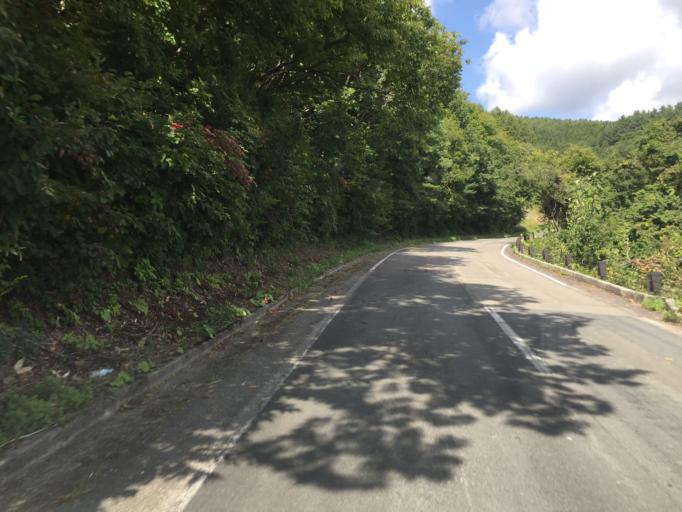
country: JP
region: Fukushima
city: Inawashiro
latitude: 37.5896
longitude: 140.0301
